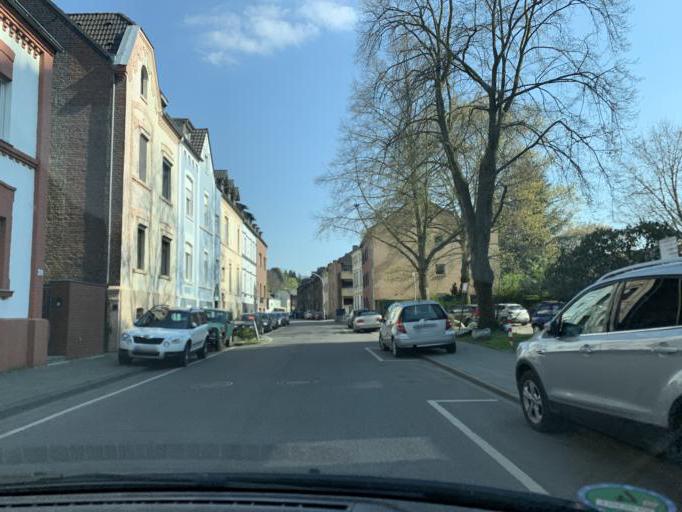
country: DE
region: North Rhine-Westphalia
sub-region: Regierungsbezirk Dusseldorf
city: Juchen
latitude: 51.1317
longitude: 6.4571
